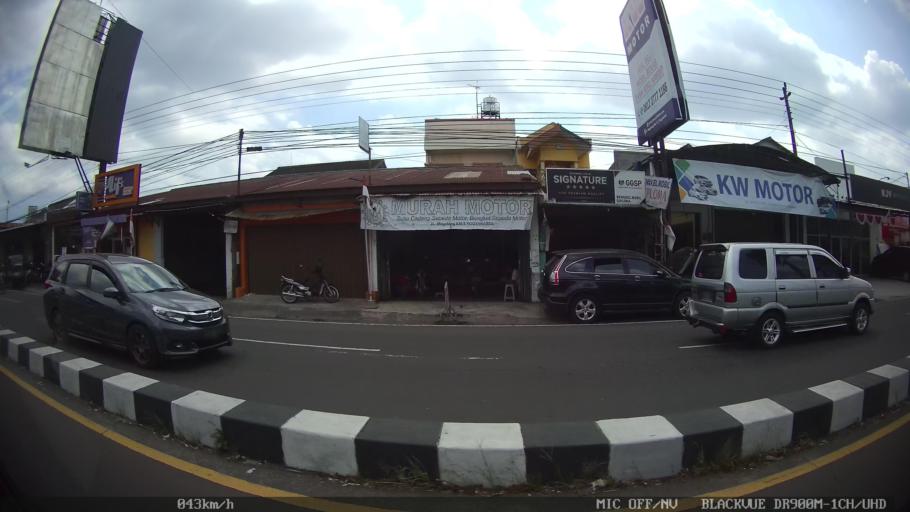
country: ID
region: Daerah Istimewa Yogyakarta
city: Yogyakarta
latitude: -7.7607
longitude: 110.3613
